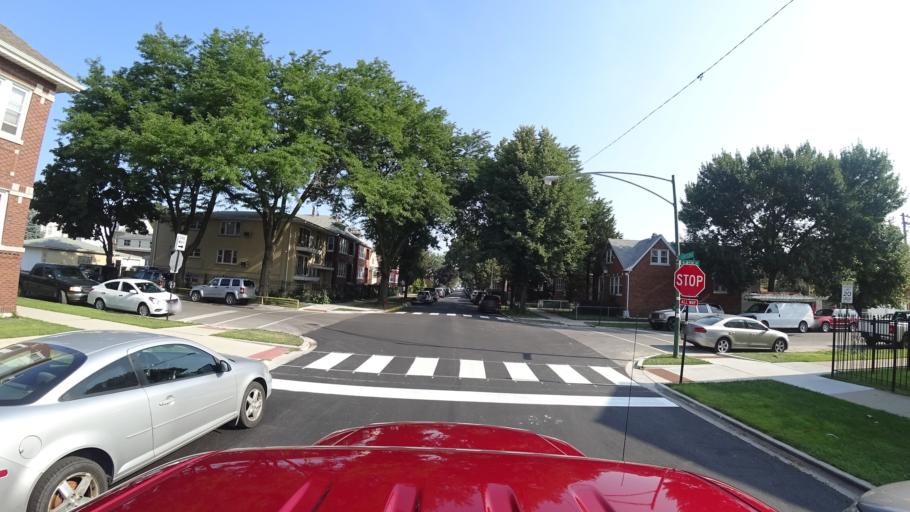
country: US
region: Illinois
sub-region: Cook County
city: Cicero
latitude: 41.8097
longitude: -87.7053
